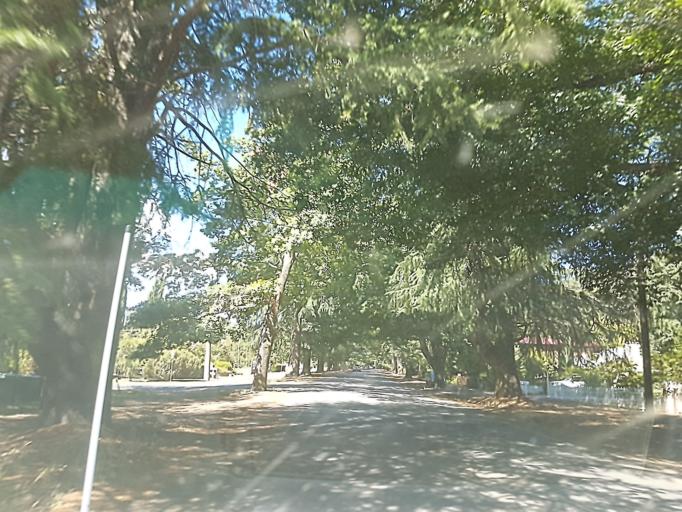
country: AU
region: Victoria
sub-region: Alpine
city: Mount Beauty
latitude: -36.7289
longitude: 146.9730
